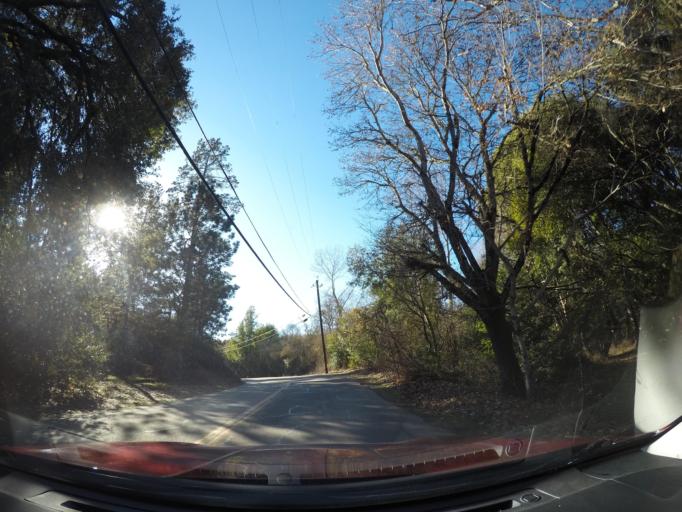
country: US
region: California
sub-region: Santa Cruz County
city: Scotts Valley
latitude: 37.0552
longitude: -122.0335
